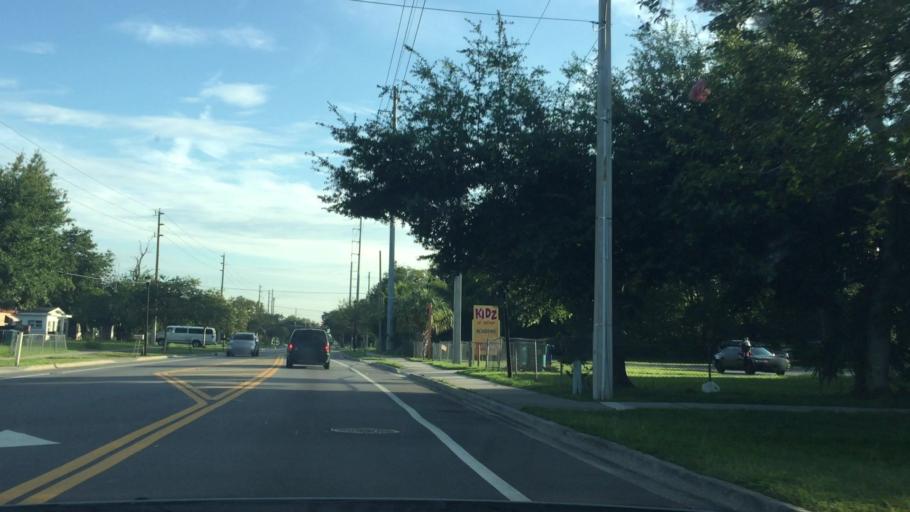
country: US
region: Florida
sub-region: Orange County
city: Pine Hills
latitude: 28.5574
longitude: -81.4304
